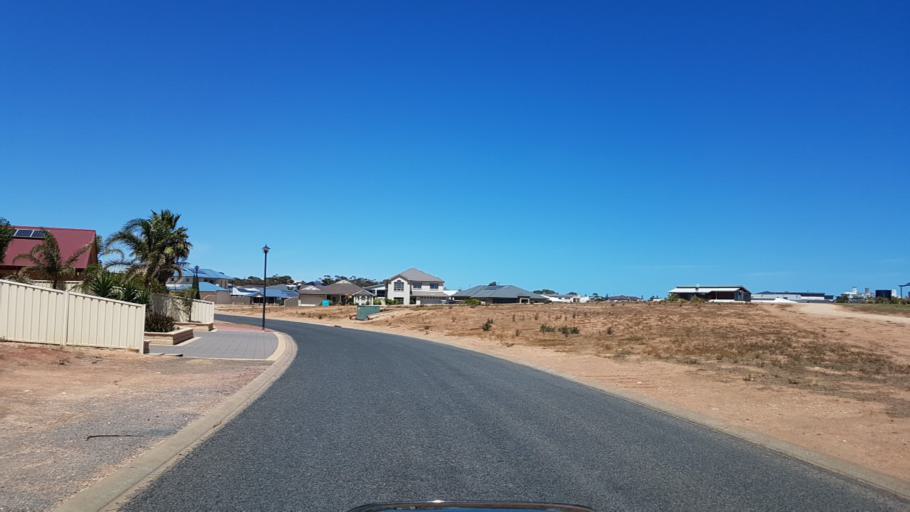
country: AU
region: South Australia
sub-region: Copper Coast
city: Wallaroo
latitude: -33.9198
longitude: 137.6384
